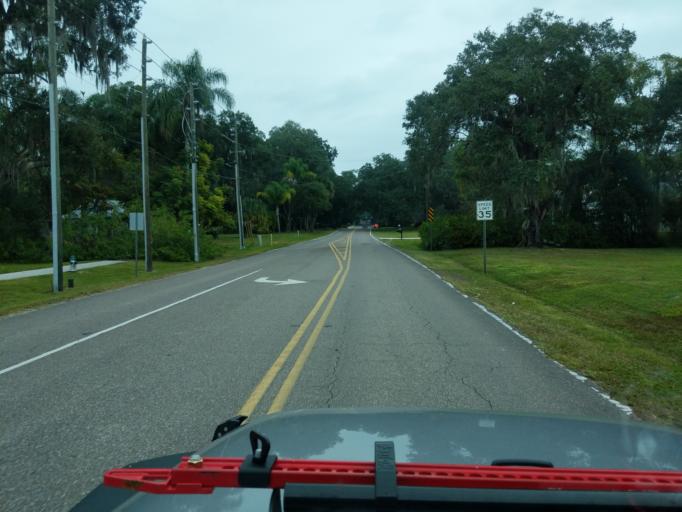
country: US
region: Florida
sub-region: Orange County
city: Oakland
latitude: 28.5547
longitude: -81.6193
